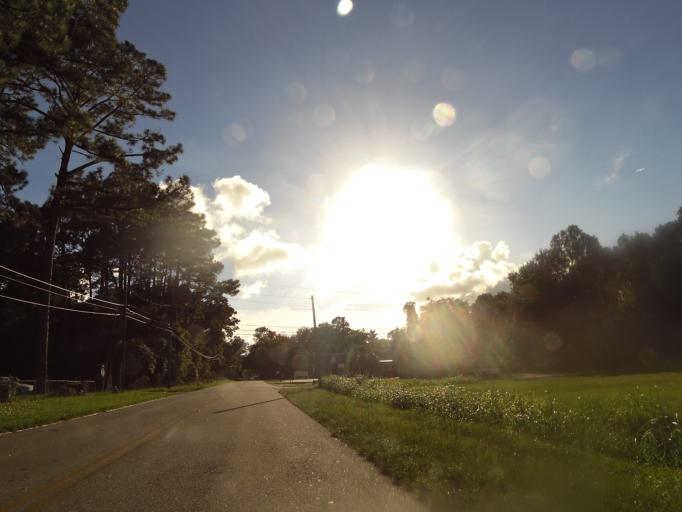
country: US
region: Georgia
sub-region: Glynn County
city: Brunswick
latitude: 31.1778
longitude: -81.4914
